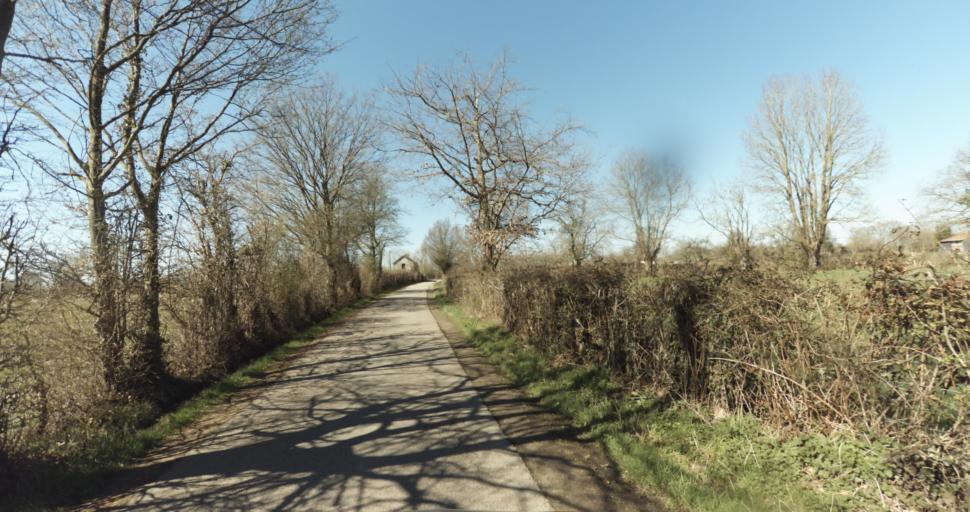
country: FR
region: Lower Normandy
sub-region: Departement du Calvados
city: Livarot
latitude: 48.9955
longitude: 0.1093
